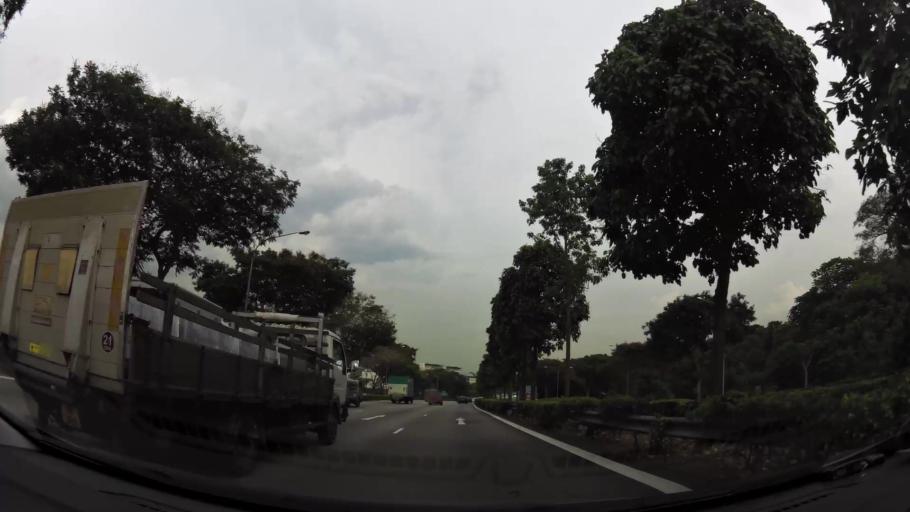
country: MY
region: Johor
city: Johor Bahru
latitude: 1.4266
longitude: 103.7829
